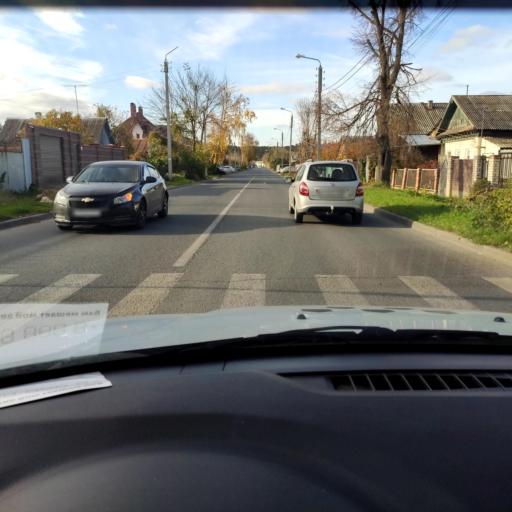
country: RU
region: Samara
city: Tol'yatti
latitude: 53.5118
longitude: 49.3990
